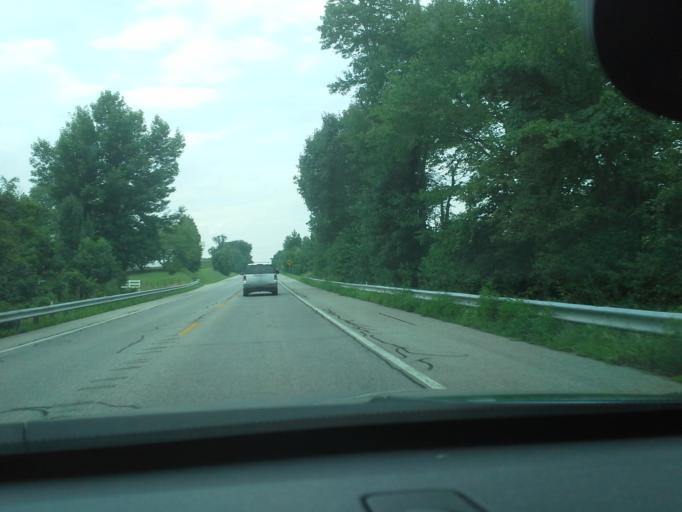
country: US
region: Maryland
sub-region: Calvert County
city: Owings
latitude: 38.7270
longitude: -76.6131
